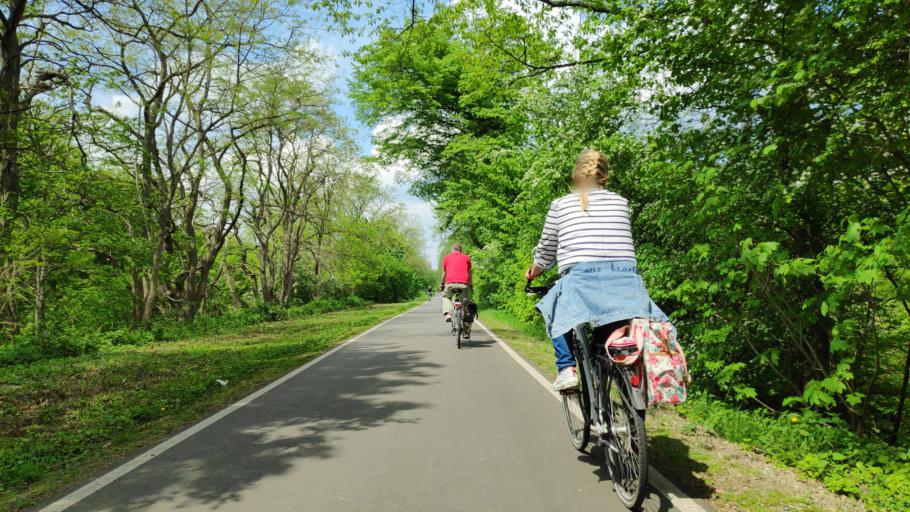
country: DE
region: North Rhine-Westphalia
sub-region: Regierungsbezirk Munster
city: Gelsenkirchen
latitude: 51.5320
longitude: 7.1333
